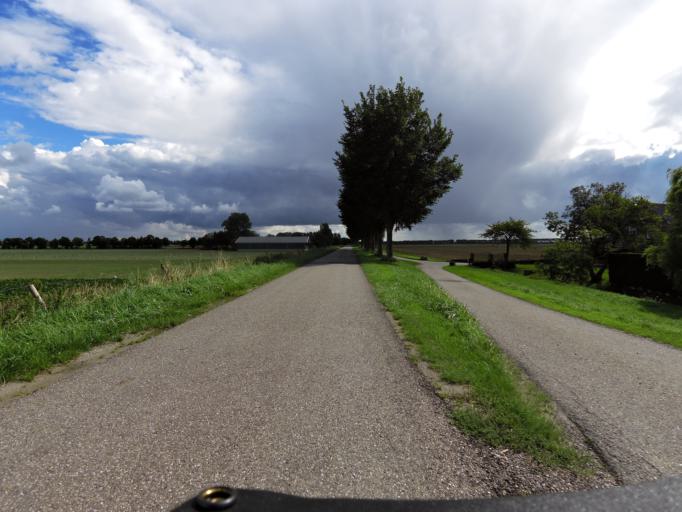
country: NL
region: North Brabant
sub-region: Gemeente Steenbergen
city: Nieuw-Vossemeer
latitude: 51.6721
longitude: 4.2613
